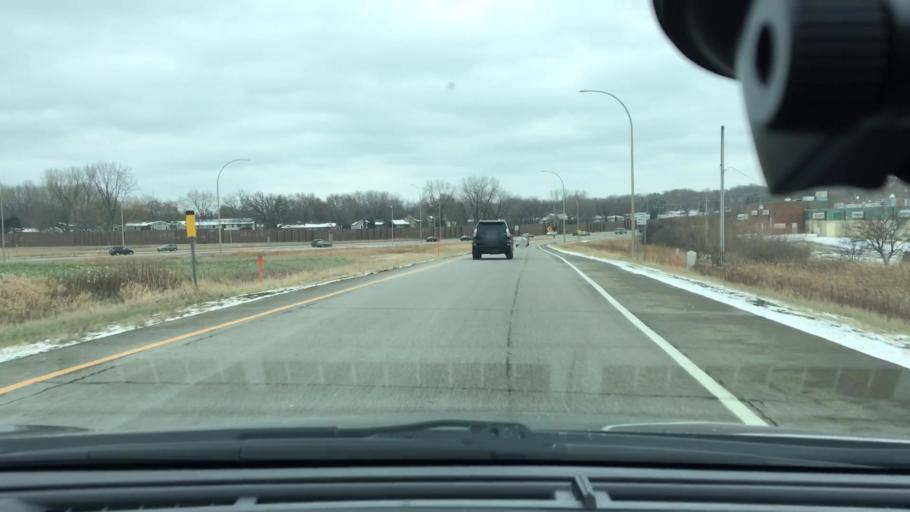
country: US
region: Minnesota
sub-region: Hennepin County
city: New Hope
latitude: 45.0327
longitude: -93.4029
